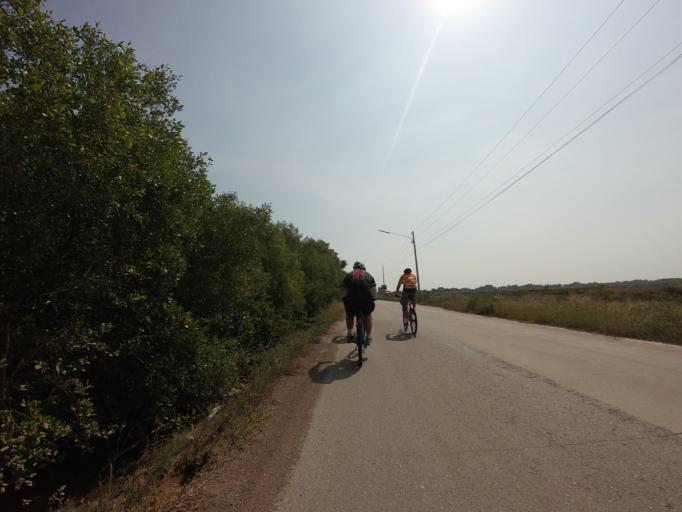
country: TH
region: Samut Sakhon
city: Samut Sakhon
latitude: 13.5061
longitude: 100.3856
